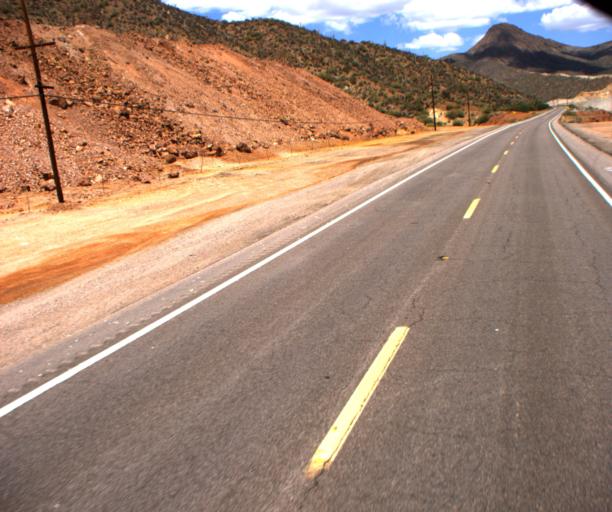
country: US
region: Arizona
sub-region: Pinal County
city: Kearny
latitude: 33.1677
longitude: -111.0075
